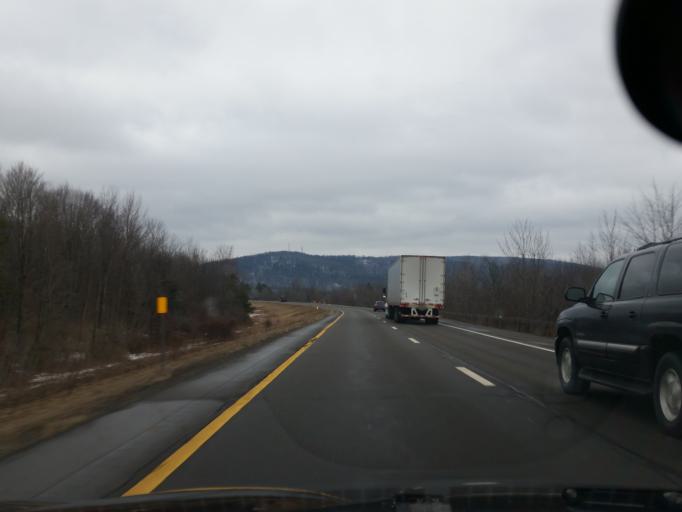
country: US
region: Pennsylvania
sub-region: Susquehanna County
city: Hallstead
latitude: 42.0243
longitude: -75.7858
